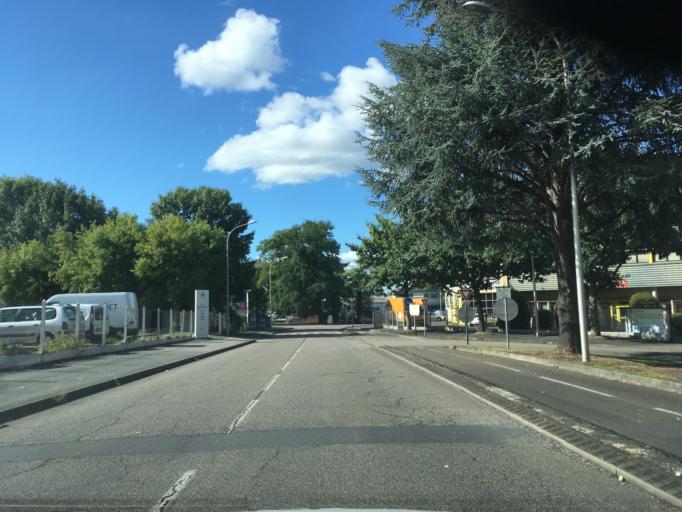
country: FR
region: Limousin
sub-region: Departement de la Correze
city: Saint-Pantaleon-de-Larche
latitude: 45.1513
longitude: 1.4886
